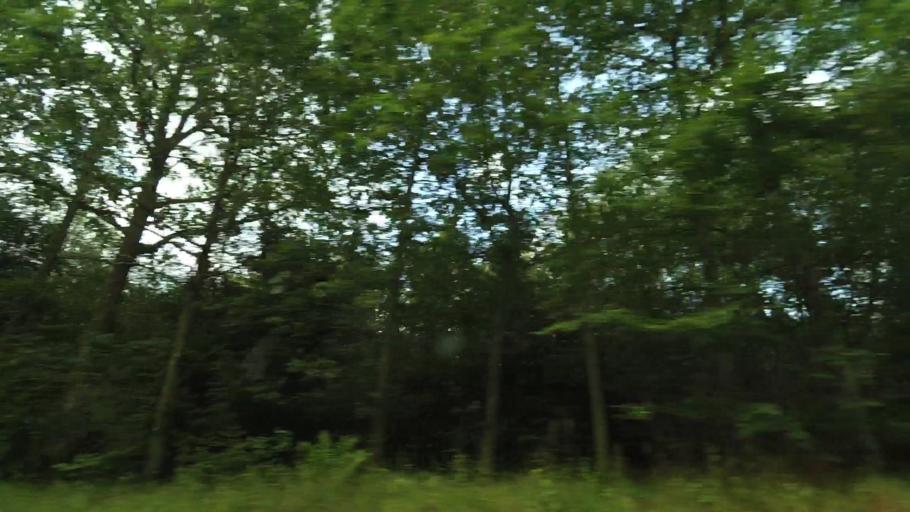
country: DK
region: Central Jutland
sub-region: Syddjurs Kommune
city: Ryomgard
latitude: 56.4183
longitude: 10.5590
